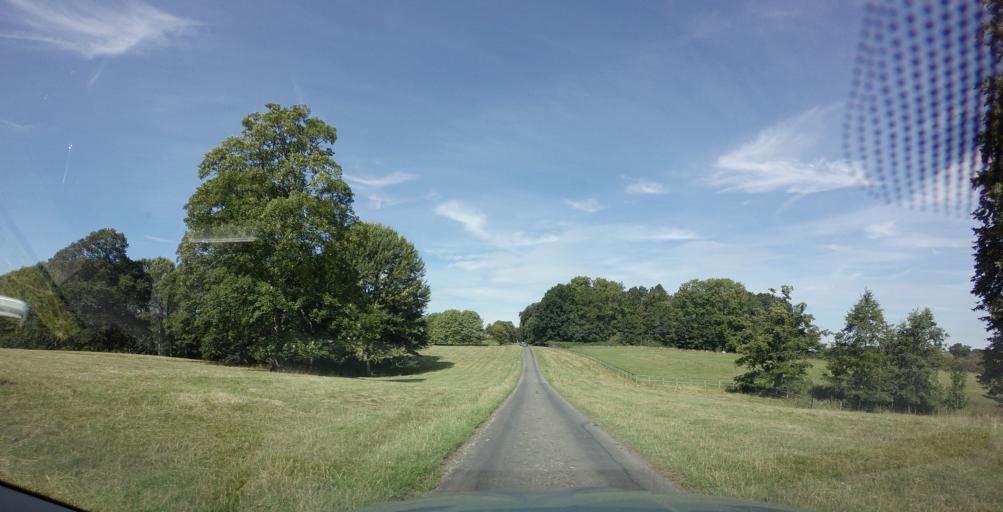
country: GB
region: England
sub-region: North Yorkshire
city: Ripon
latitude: 54.1073
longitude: -1.4691
